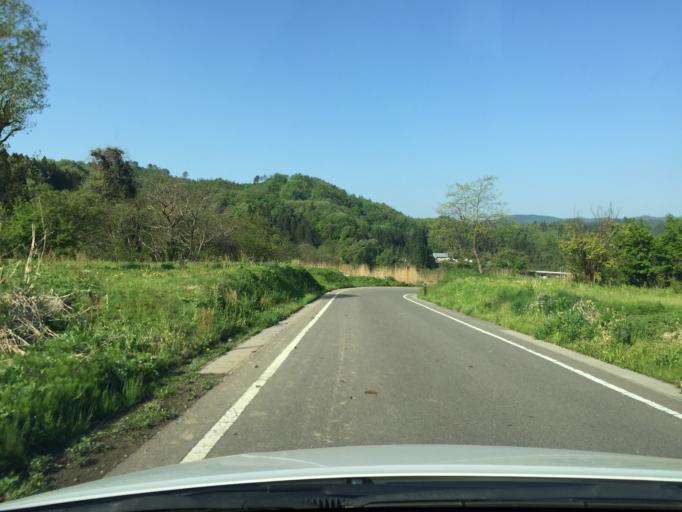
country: JP
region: Fukushima
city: Kitakata
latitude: 37.6759
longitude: 139.7986
